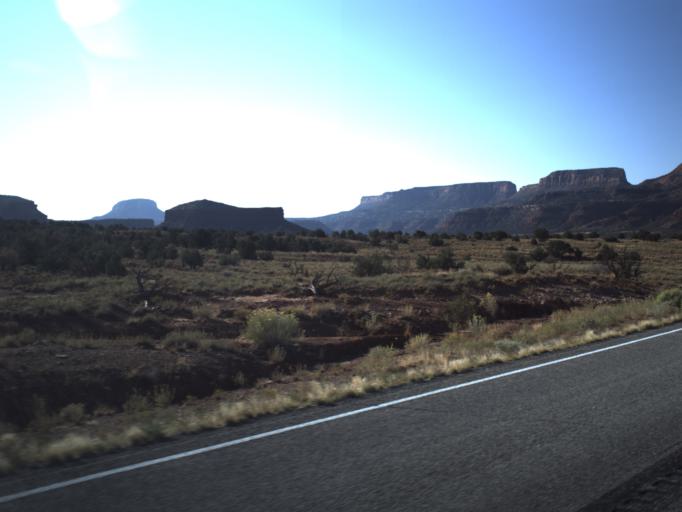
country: US
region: Utah
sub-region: San Juan County
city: Blanding
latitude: 37.6477
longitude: -110.1433
